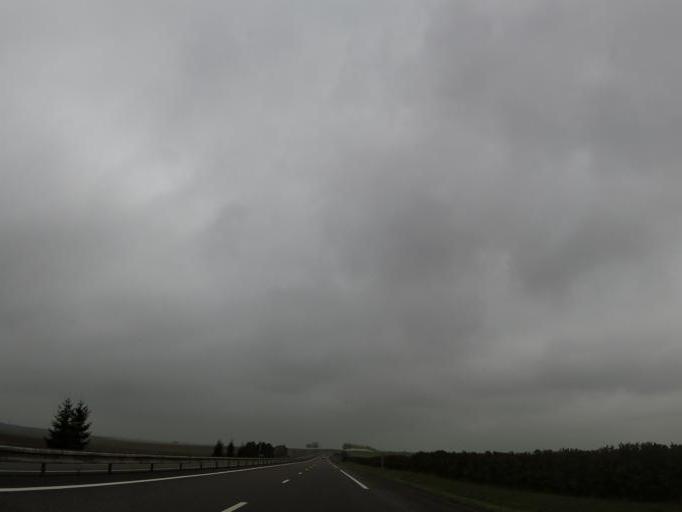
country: FR
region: Champagne-Ardenne
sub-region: Departement de la Marne
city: Courtisols
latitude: 49.0338
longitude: 4.4496
